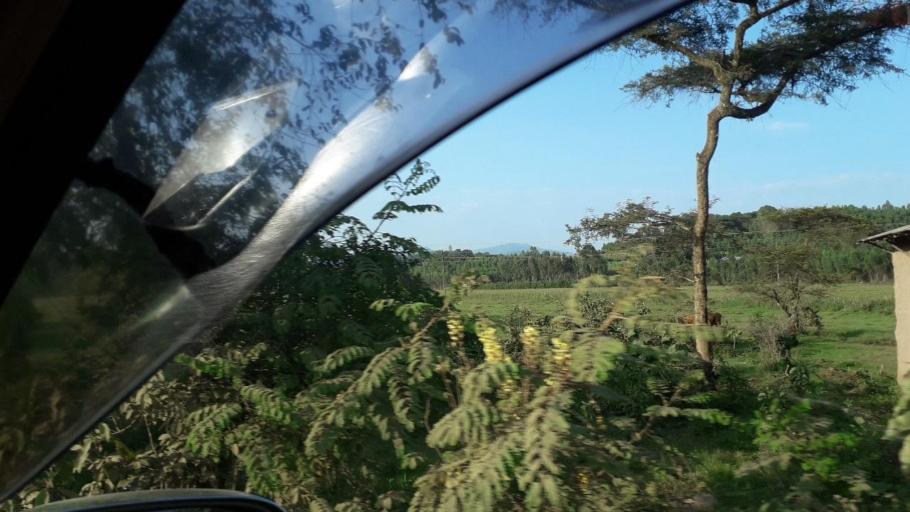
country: ET
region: Oromiya
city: Jima
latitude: 7.5941
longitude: 36.8512
